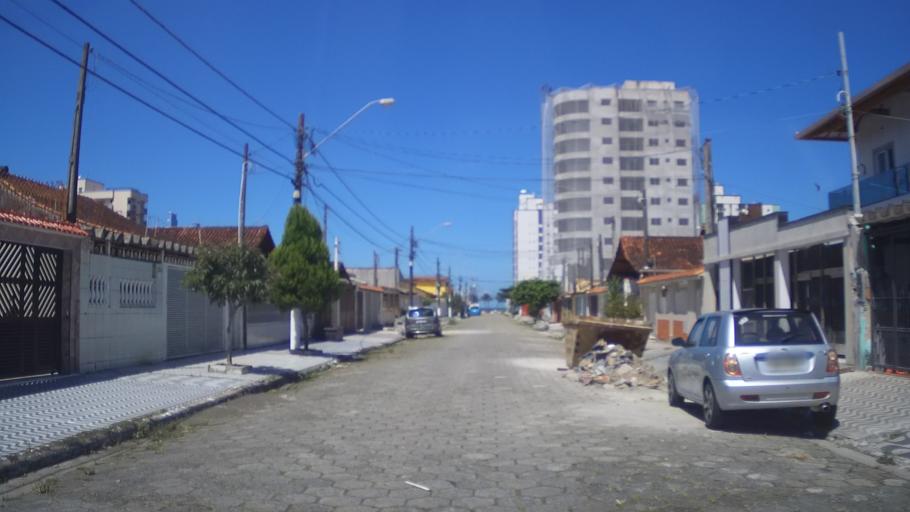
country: BR
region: Sao Paulo
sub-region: Praia Grande
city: Praia Grande
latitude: -24.0415
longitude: -46.5110
